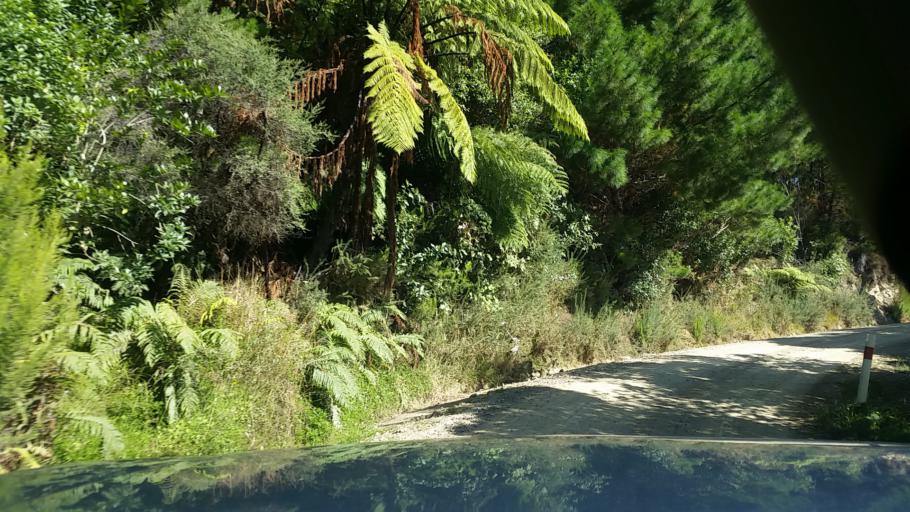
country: NZ
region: Marlborough
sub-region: Marlborough District
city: Picton
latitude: -41.2997
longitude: 174.1858
